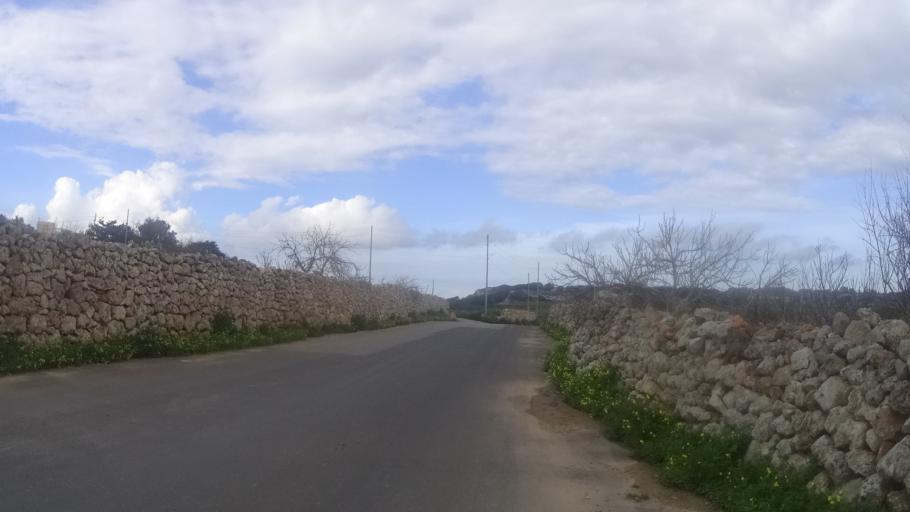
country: MT
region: L-Imtarfa
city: Imtarfa
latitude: 35.9014
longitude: 14.3788
